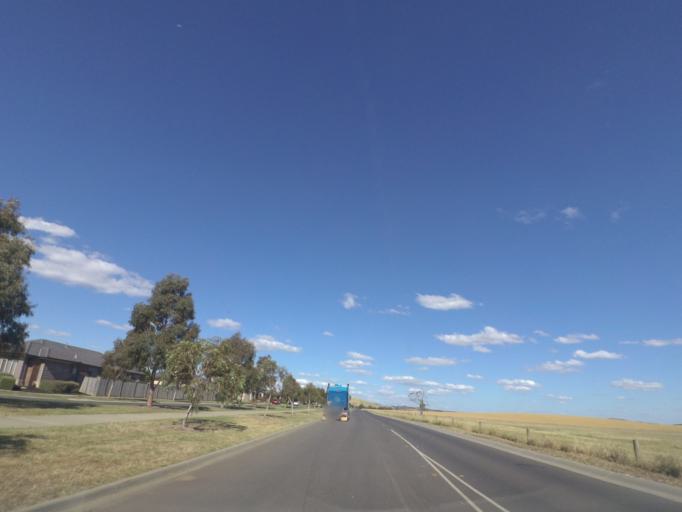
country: AU
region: Victoria
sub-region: Whittlesea
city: Whittlesea
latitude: -37.4215
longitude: 144.9651
